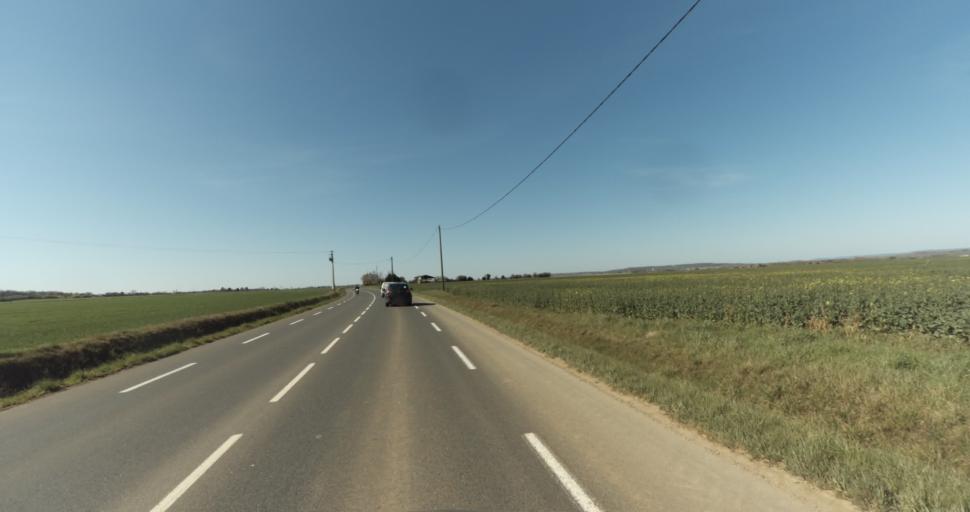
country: FR
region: Lower Normandy
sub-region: Departement du Calvados
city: Saint-Pierre-sur-Dives
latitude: 49.0311
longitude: -0.0588
